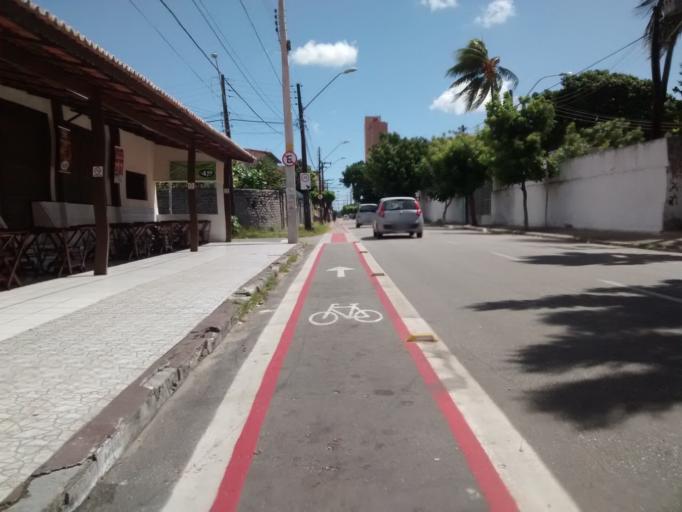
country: BR
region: Ceara
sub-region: Fortaleza
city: Fortaleza
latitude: -3.7396
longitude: -38.5565
